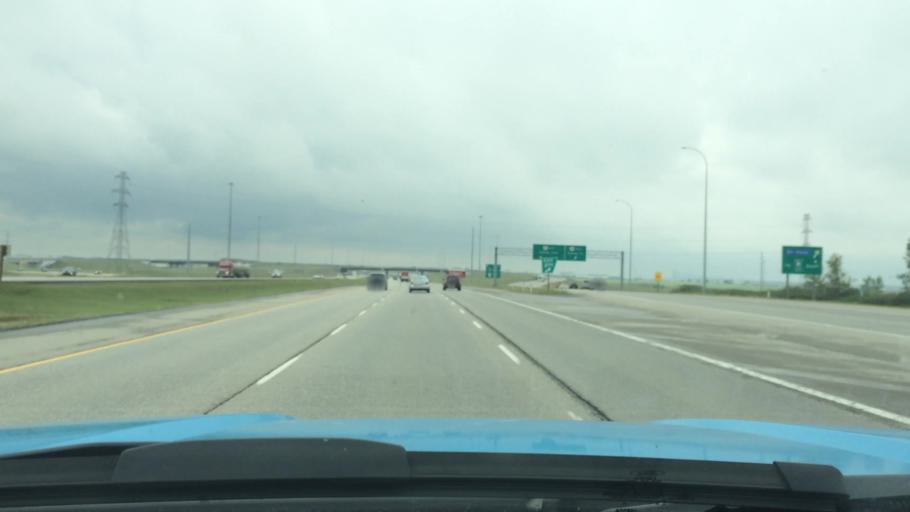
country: CA
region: Alberta
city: Airdrie
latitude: 51.1837
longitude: -114.0018
